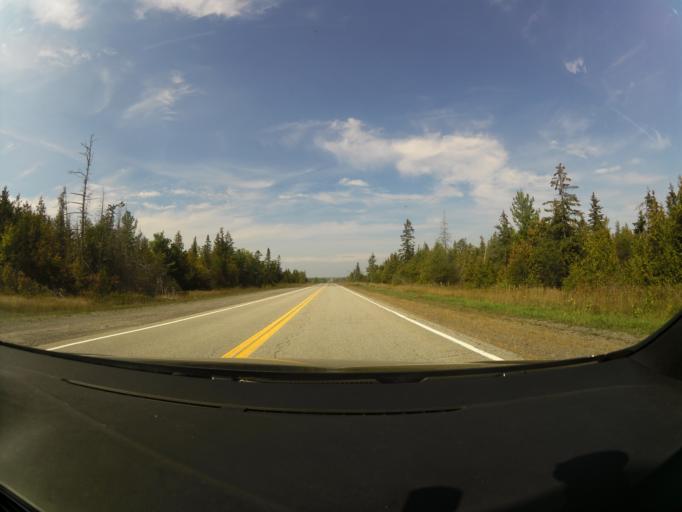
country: CA
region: Ontario
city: Arnprior
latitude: 45.3436
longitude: -76.1979
